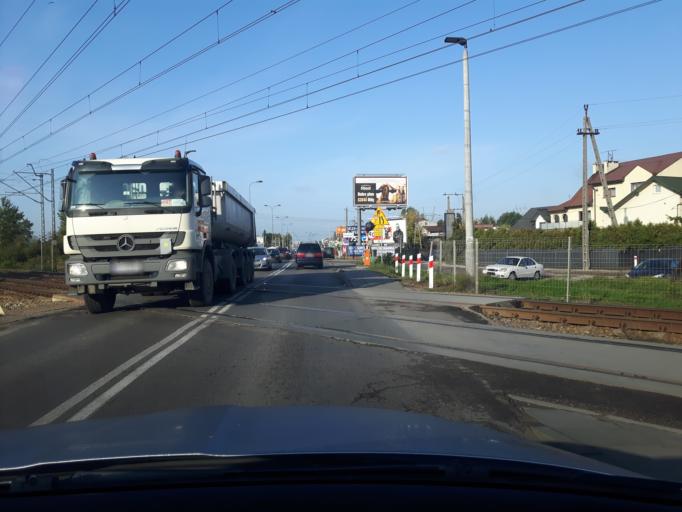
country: PL
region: Masovian Voivodeship
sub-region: Powiat wolominski
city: Zabki
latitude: 52.2861
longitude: 21.0990
